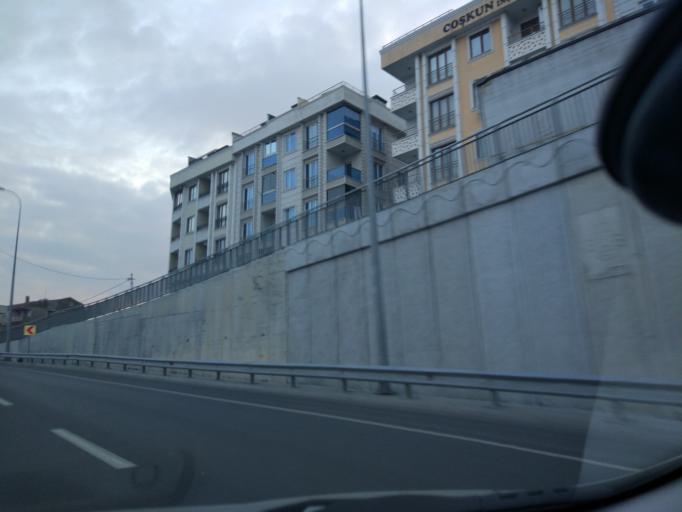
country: TR
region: Istanbul
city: Yakuplu
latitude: 41.0002
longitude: 28.6764
